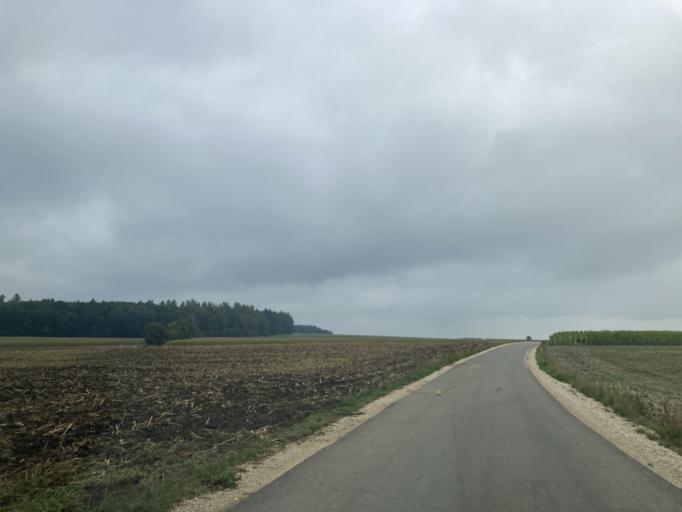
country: DE
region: Bavaria
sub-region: Swabia
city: Medlingen
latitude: 48.5710
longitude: 10.3021
